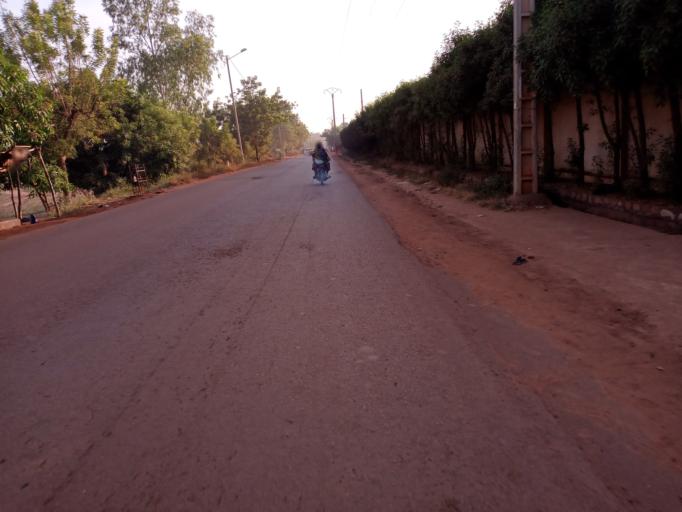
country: ML
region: Bamako
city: Bamako
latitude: 12.6321
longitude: -7.9413
